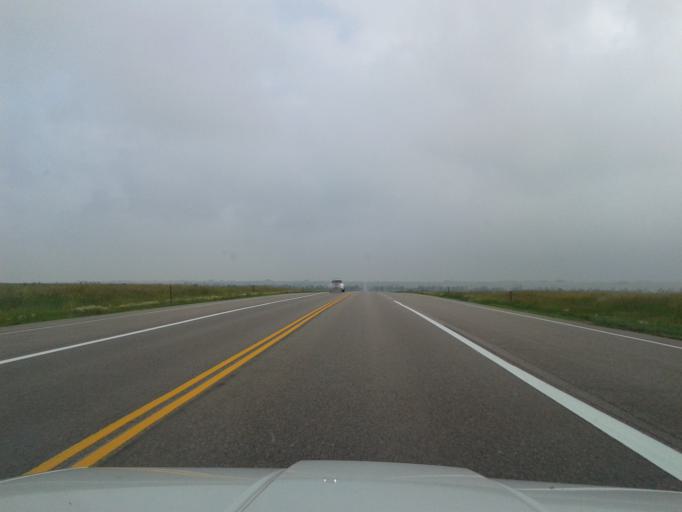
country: US
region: Colorado
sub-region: Elbert County
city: Ponderosa Park
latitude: 39.3138
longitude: -104.7351
